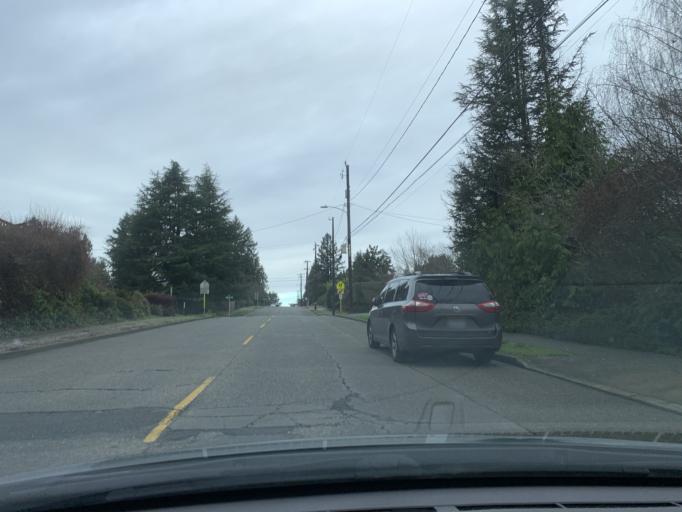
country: US
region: Washington
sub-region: King County
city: White Center
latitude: 47.5703
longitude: -122.3953
